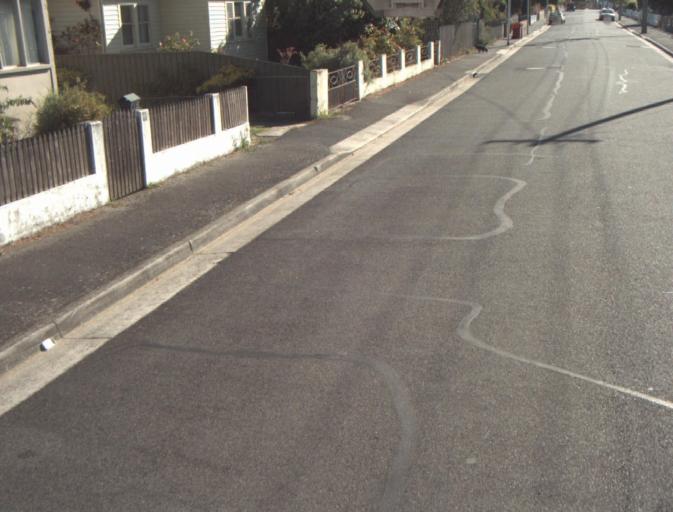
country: AU
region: Tasmania
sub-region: Launceston
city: Newnham
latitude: -41.4061
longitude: 147.1275
